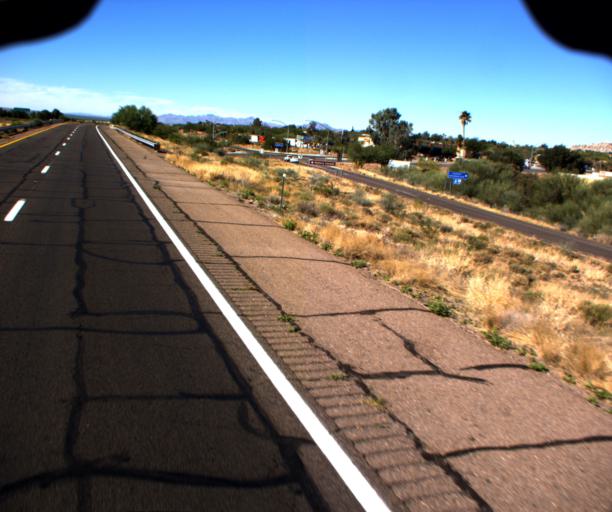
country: US
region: Arizona
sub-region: Pima County
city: Green Valley
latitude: 31.8531
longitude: -110.9935
